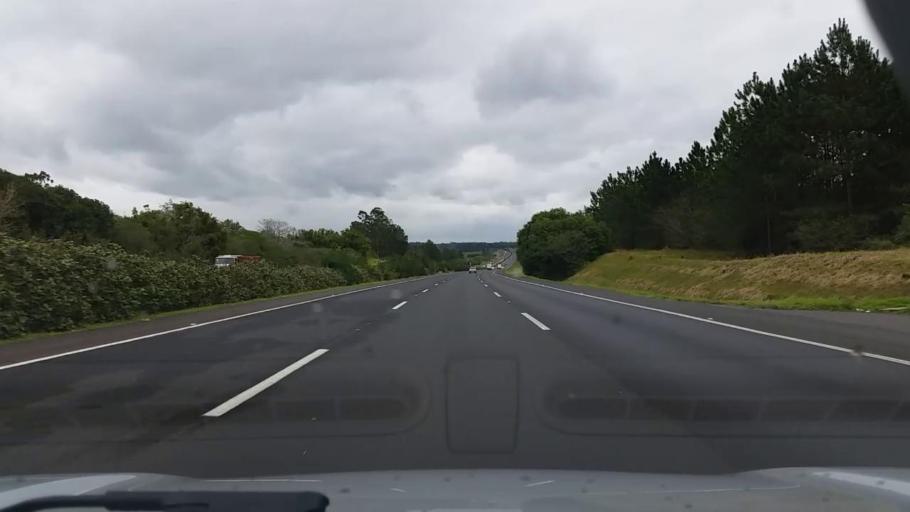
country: BR
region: Rio Grande do Sul
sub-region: Gravatai
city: Gravatai
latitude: -29.9196
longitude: -50.8316
